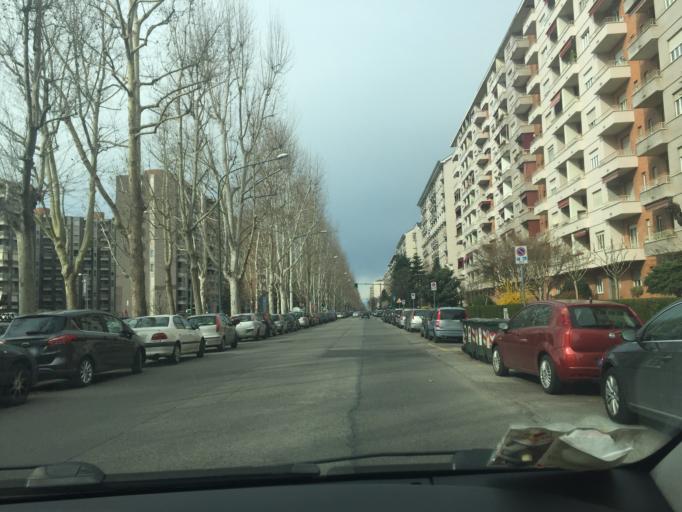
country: IT
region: Piedmont
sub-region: Provincia di Torino
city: Lesna
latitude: 45.0654
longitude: 7.6316
